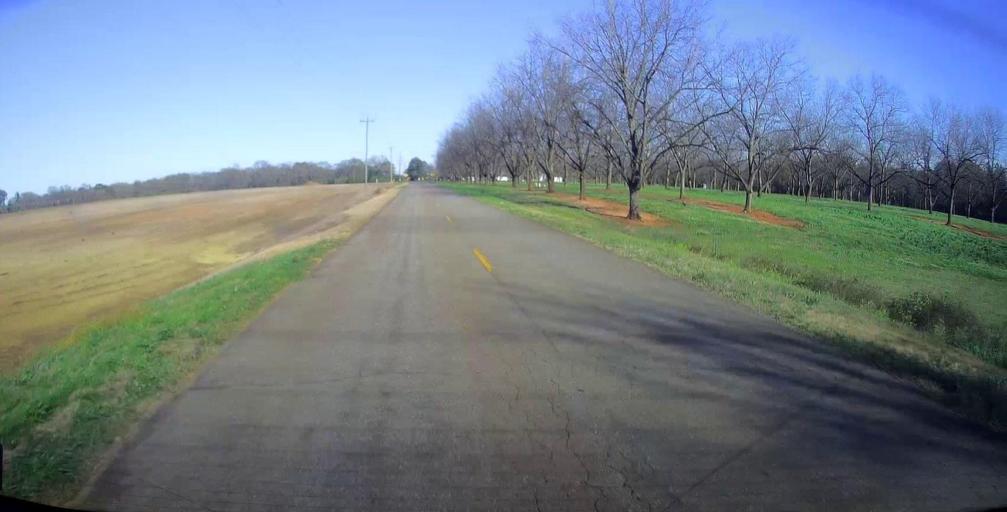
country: US
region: Georgia
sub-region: Macon County
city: Marshallville
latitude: 32.5116
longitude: -83.9286
